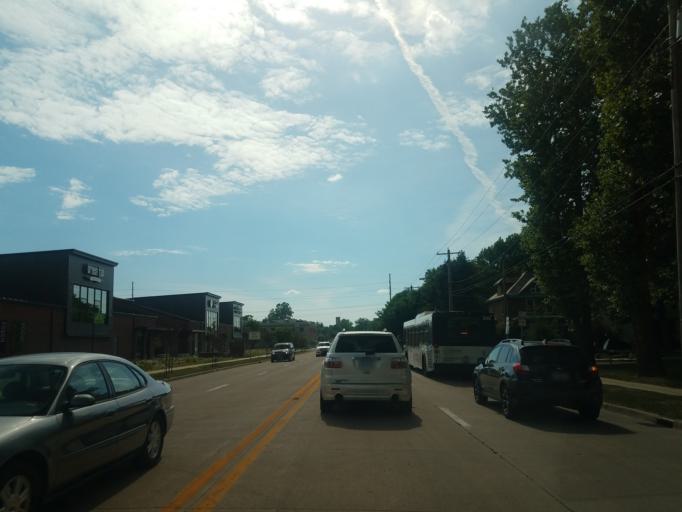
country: US
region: Illinois
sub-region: McLean County
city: Bloomington
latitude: 40.4799
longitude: -88.9801
